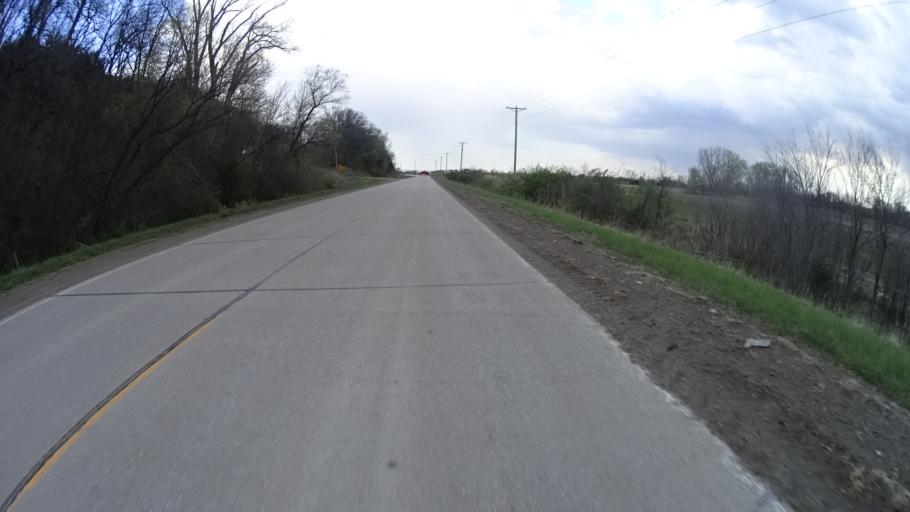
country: US
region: Iowa
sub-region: Mills County
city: Glenwood
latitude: 41.0762
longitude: -95.8133
